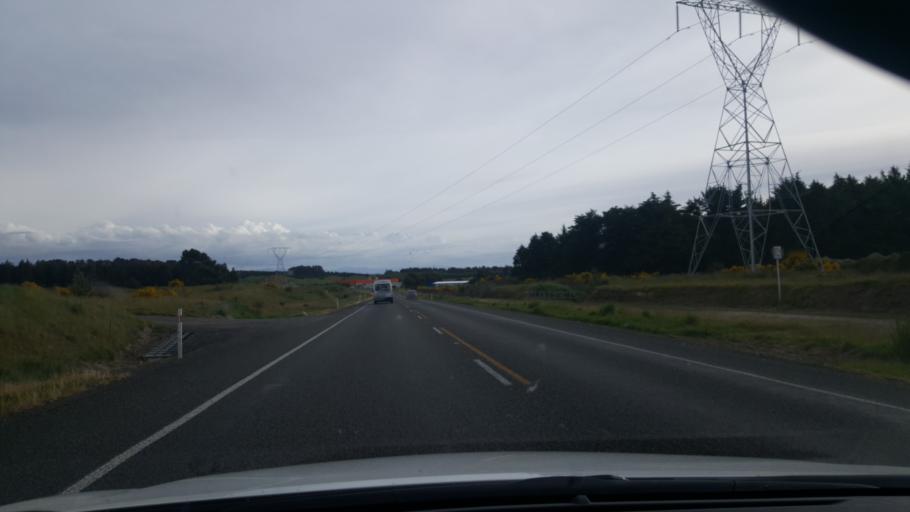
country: NZ
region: Waikato
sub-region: Taupo District
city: Taupo
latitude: -38.6959
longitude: 176.1133
